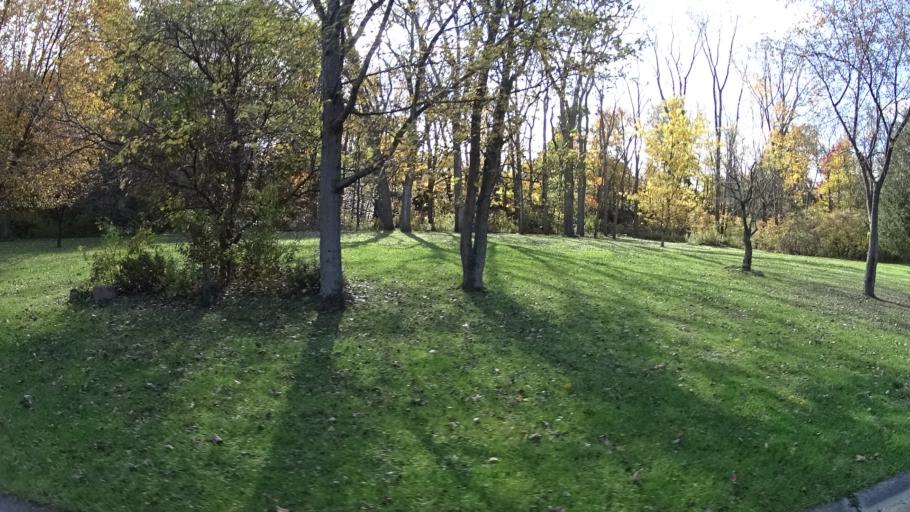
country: US
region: Ohio
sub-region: Lorain County
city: Lorain
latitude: 41.4460
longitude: -82.2171
